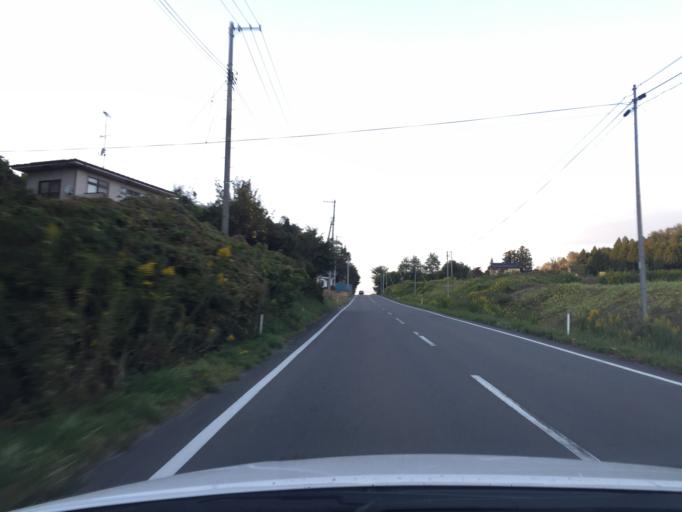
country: JP
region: Fukushima
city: Sukagawa
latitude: 37.3247
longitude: 140.4402
